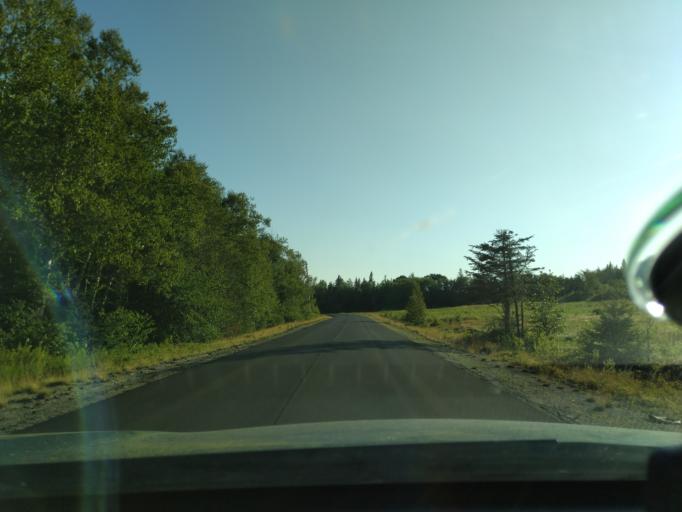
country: US
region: Maine
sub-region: Washington County
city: East Machias
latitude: 44.7062
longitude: -67.1489
